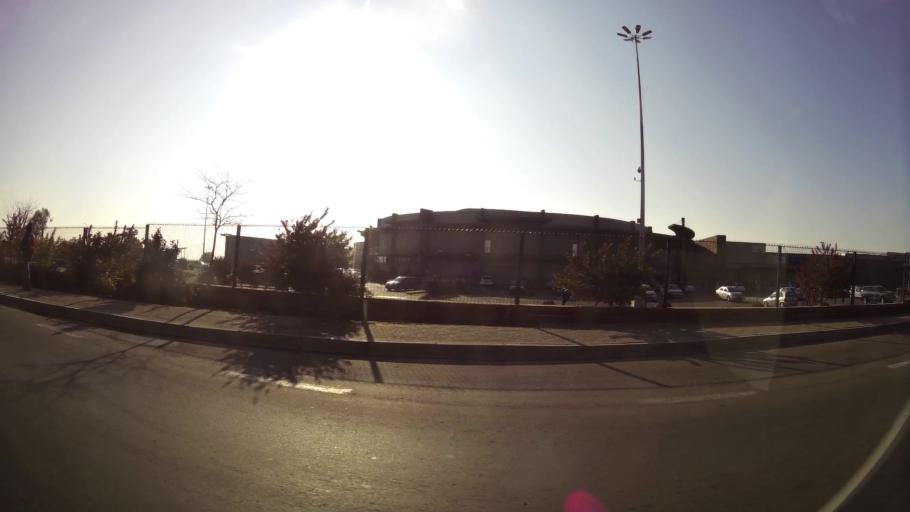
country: ZA
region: Orange Free State
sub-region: Mangaung Metropolitan Municipality
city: Bloemfontein
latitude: -29.1589
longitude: 26.2554
